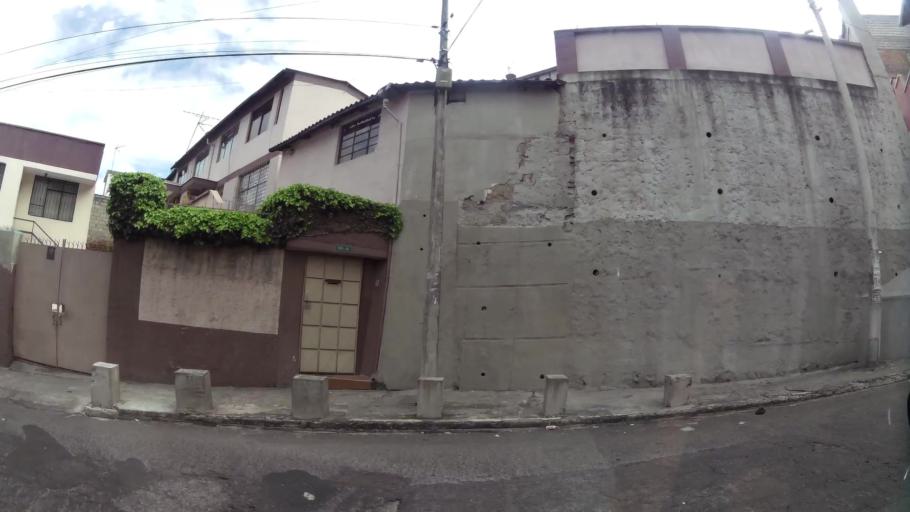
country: EC
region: Pichincha
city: Quito
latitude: -0.2168
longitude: -78.4870
